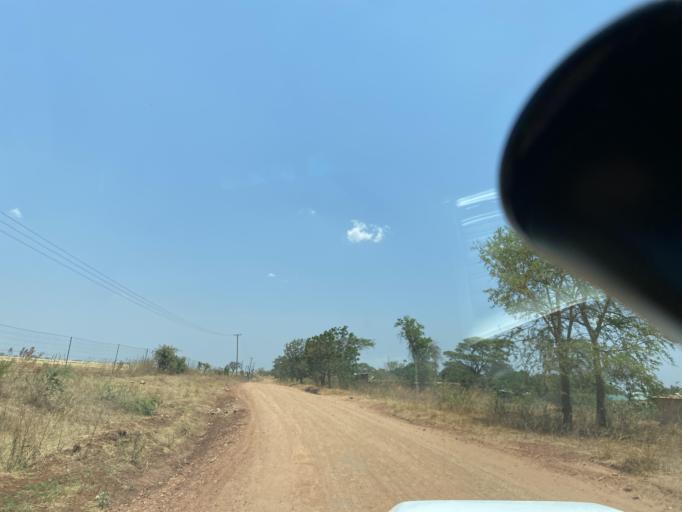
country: ZM
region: Lusaka
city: Lusaka
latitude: -15.4515
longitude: 28.0498
